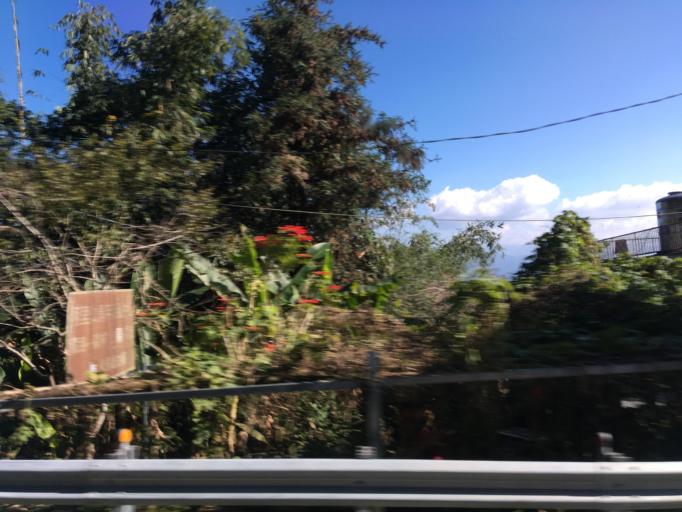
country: TW
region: Taiwan
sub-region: Chiayi
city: Jiayi Shi
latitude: 23.4088
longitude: 120.6539
